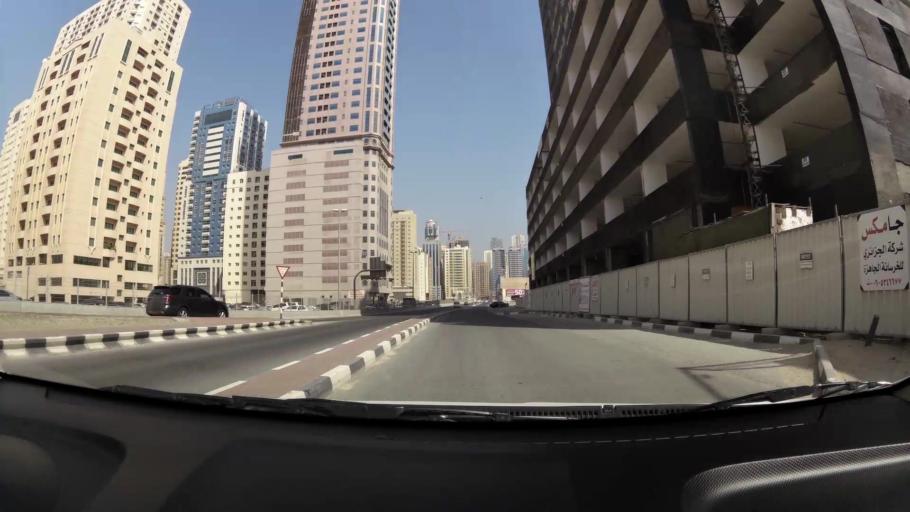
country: AE
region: Ash Shariqah
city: Sharjah
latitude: 25.3053
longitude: 55.3835
